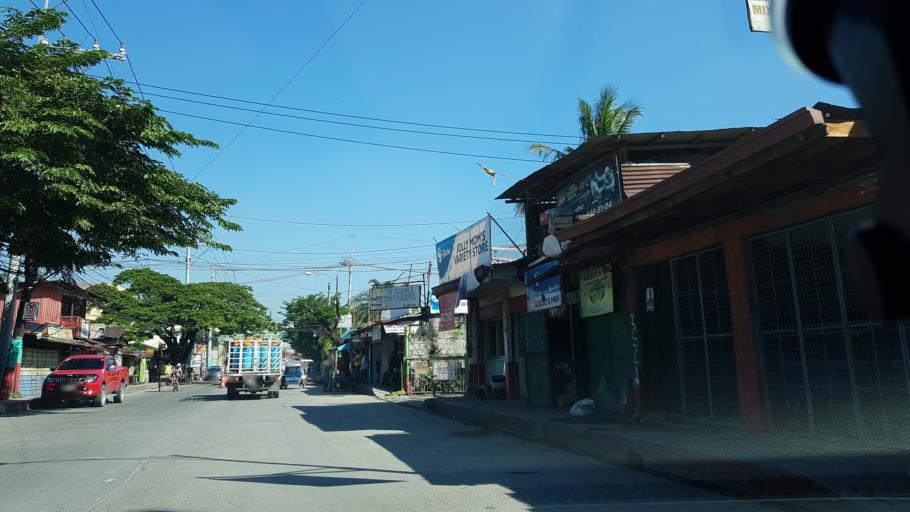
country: PH
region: Calabarzon
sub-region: Province of Rizal
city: Pateros
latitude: 14.5606
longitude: 121.0948
